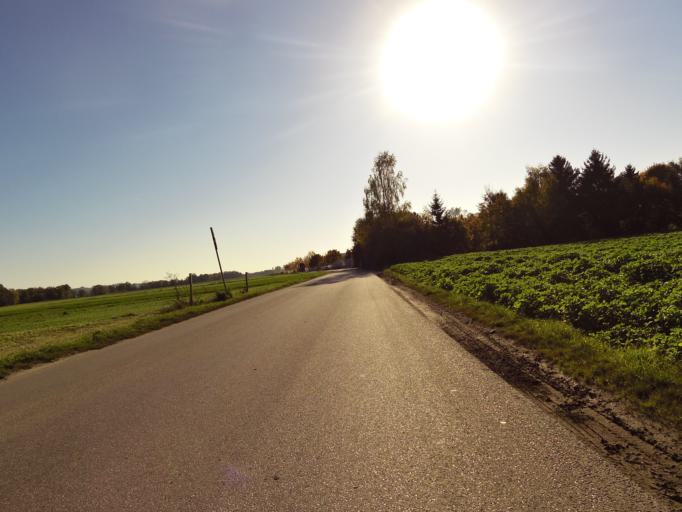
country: DE
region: Bavaria
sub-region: Lower Bavaria
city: Bruckberg
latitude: 48.4808
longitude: 12.0011
